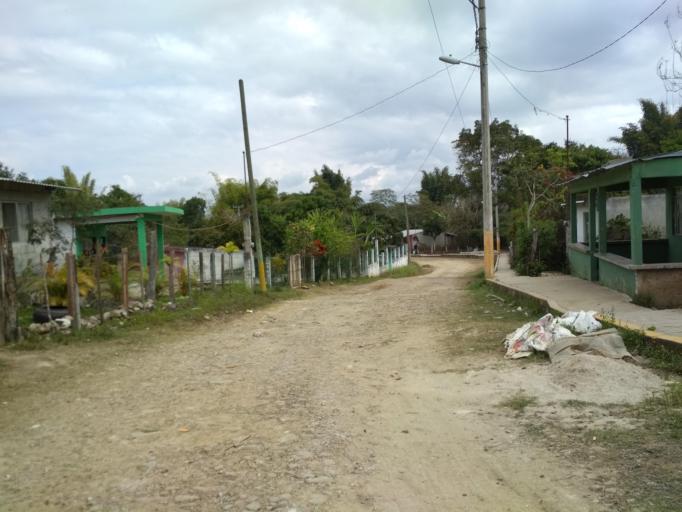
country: MX
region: Veracruz
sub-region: Coatepec
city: Tuzamapan
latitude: 19.3675
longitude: -96.8801
